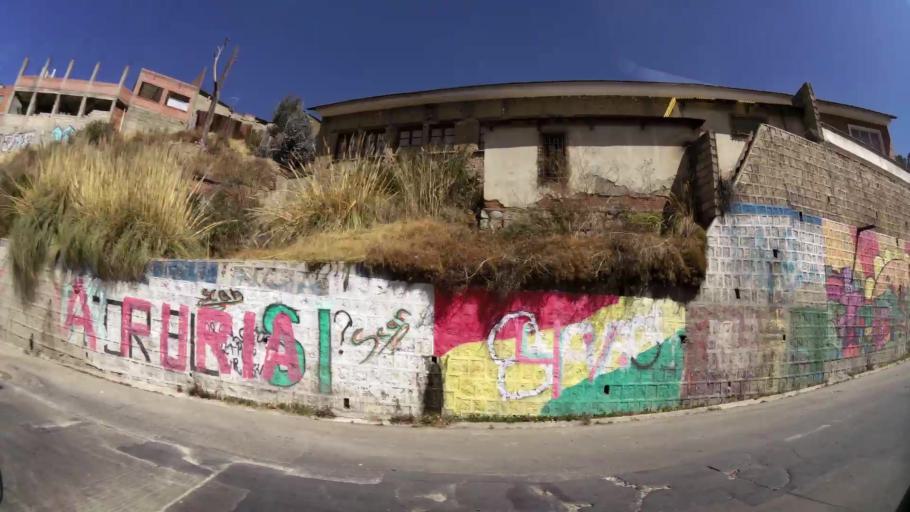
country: BO
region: La Paz
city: La Paz
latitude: -16.4784
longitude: -68.1515
